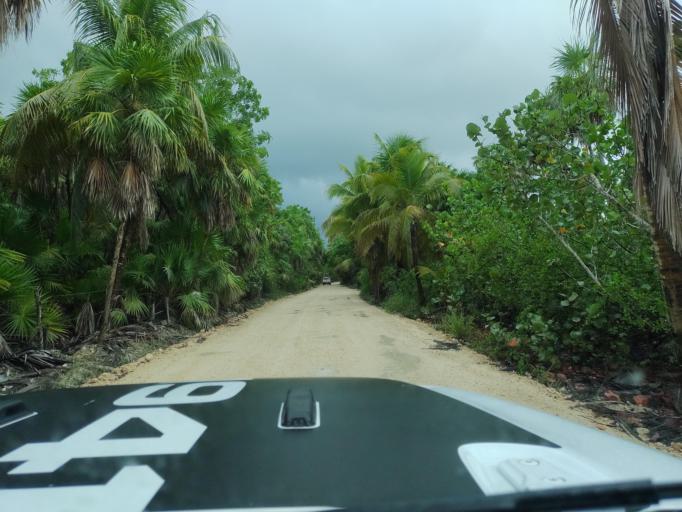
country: MX
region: Quintana Roo
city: Tulum
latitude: 20.0697
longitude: -87.4789
